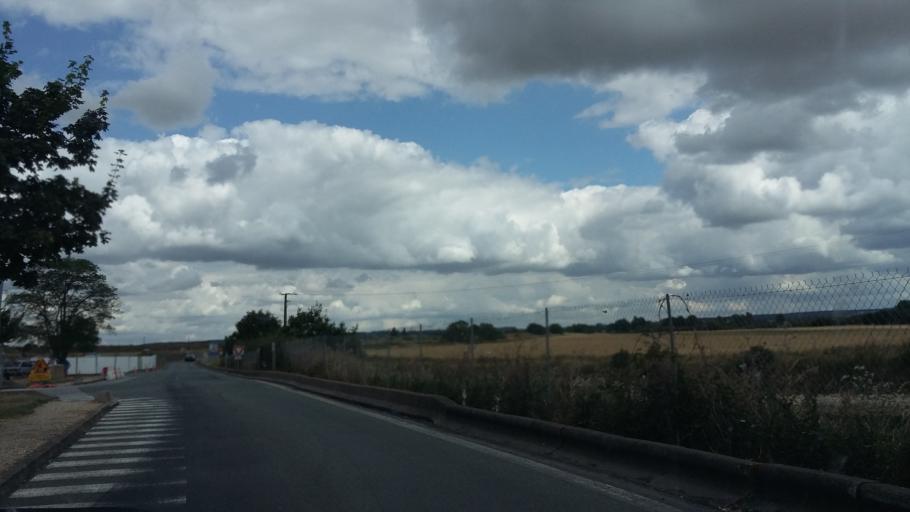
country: FR
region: Poitou-Charentes
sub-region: Departement de la Vienne
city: Jaunay-Clan
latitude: 46.7023
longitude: 0.3725
